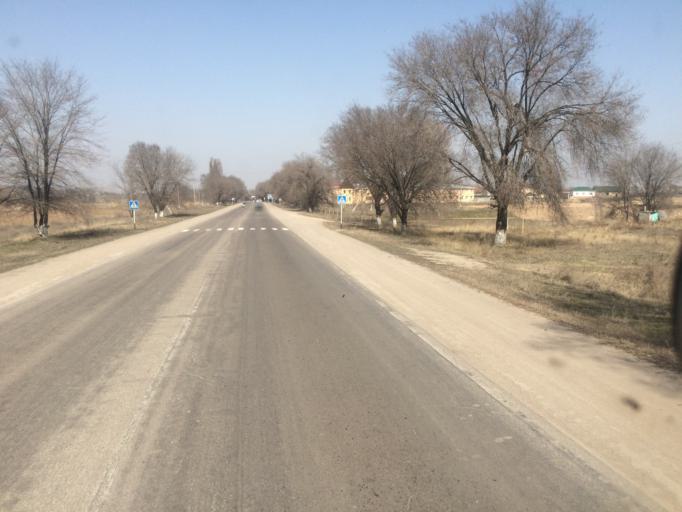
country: KZ
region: Almaty Oblysy
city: Burunday
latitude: 43.2969
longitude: 76.6729
